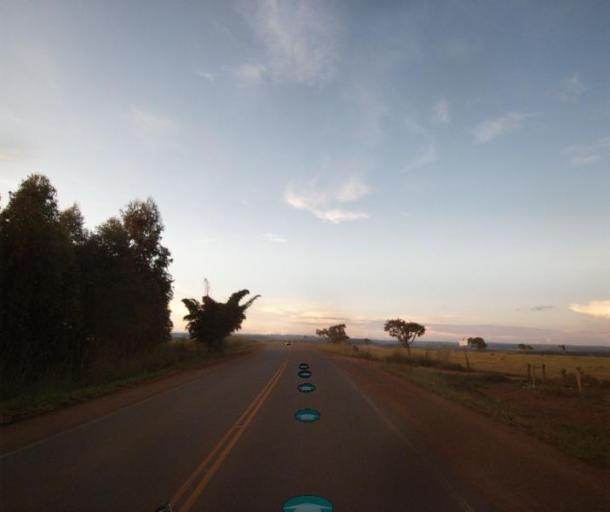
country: BR
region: Goias
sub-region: Pirenopolis
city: Pirenopolis
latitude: -16.0182
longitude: -48.8374
